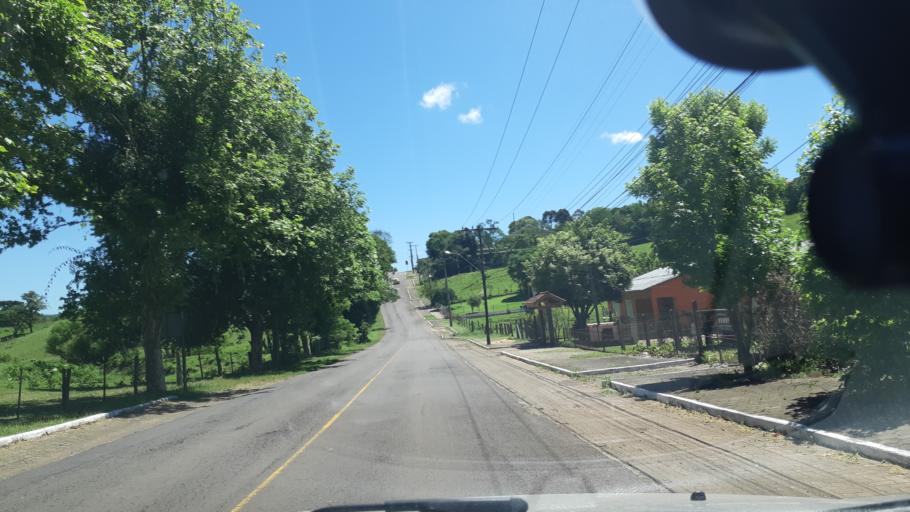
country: BR
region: Rio Grande do Sul
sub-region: Novo Hamburgo
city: Novo Hamburgo
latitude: -29.6267
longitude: -51.0942
